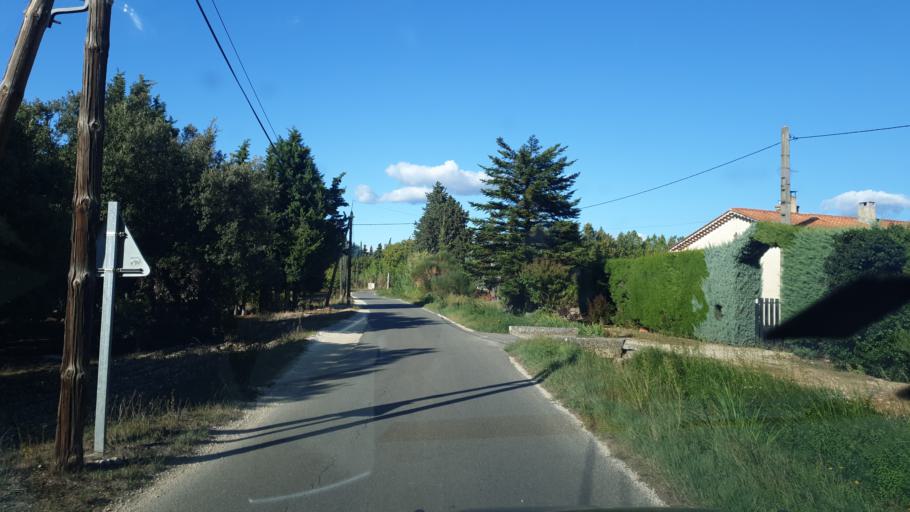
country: FR
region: Provence-Alpes-Cote d'Azur
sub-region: Departement du Vaucluse
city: Monteux
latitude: 44.0464
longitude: 5.0078
